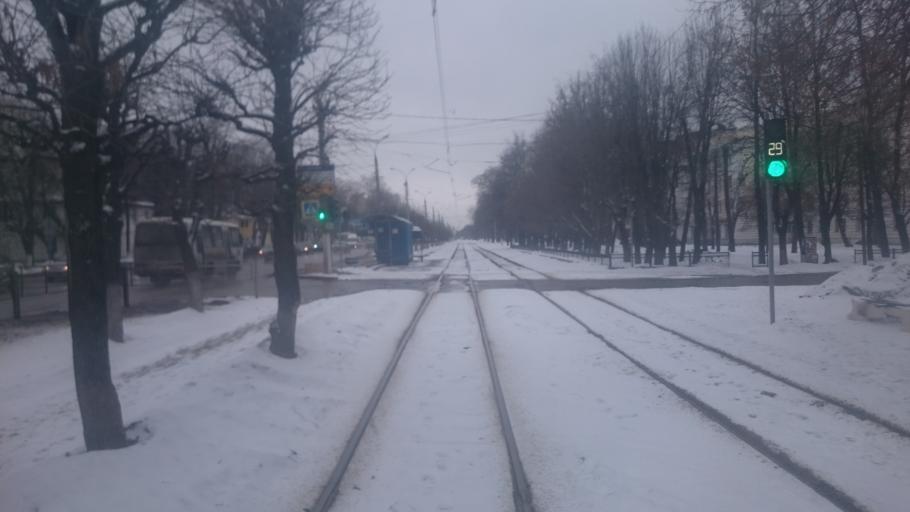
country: RU
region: Tverskaya
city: Tver
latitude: 56.8723
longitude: 35.8622
